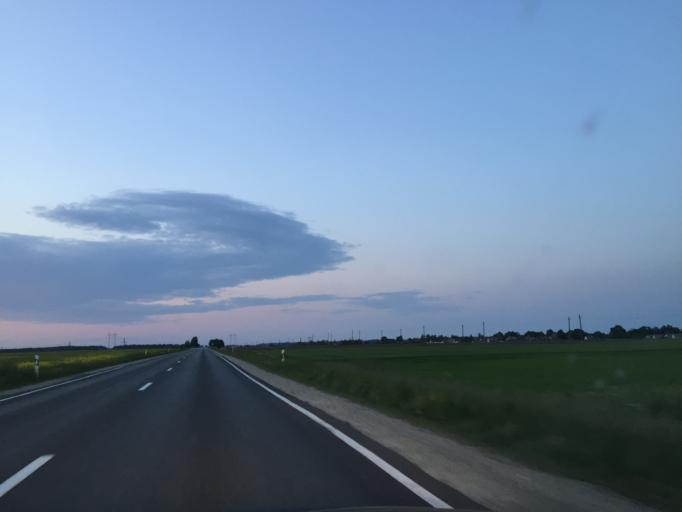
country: LT
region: Siauliu apskritis
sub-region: Joniskis
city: Joniskis
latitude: 56.0994
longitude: 23.4785
